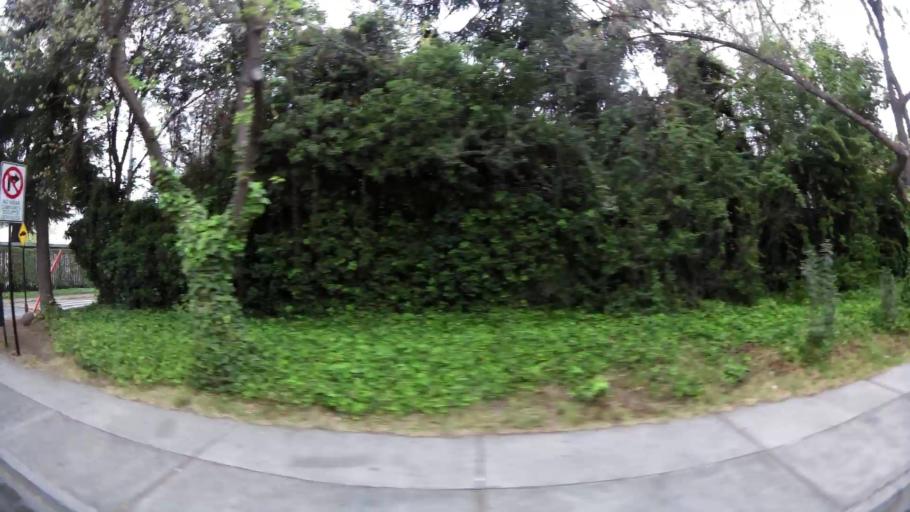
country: CL
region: Santiago Metropolitan
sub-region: Provincia de Santiago
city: Villa Presidente Frei, Nunoa, Santiago, Chile
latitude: -33.3966
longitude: -70.5761
